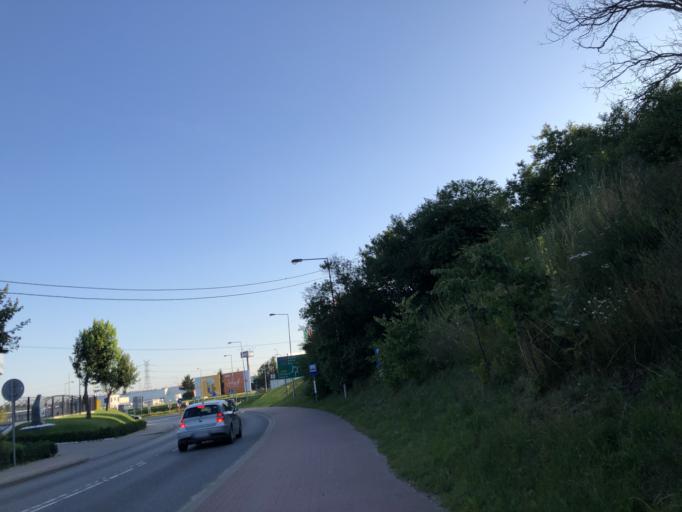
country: PL
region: Pomeranian Voivodeship
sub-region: Powiat gdanski
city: Rotmanka
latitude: 54.2809
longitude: 18.5947
